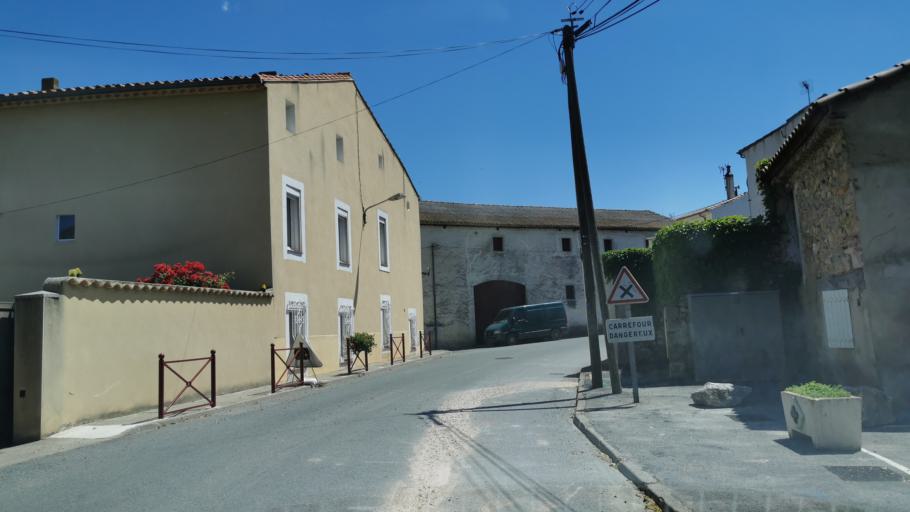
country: FR
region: Languedoc-Roussillon
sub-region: Departement de l'Aude
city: Ginestas
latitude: 43.2449
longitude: 2.8933
